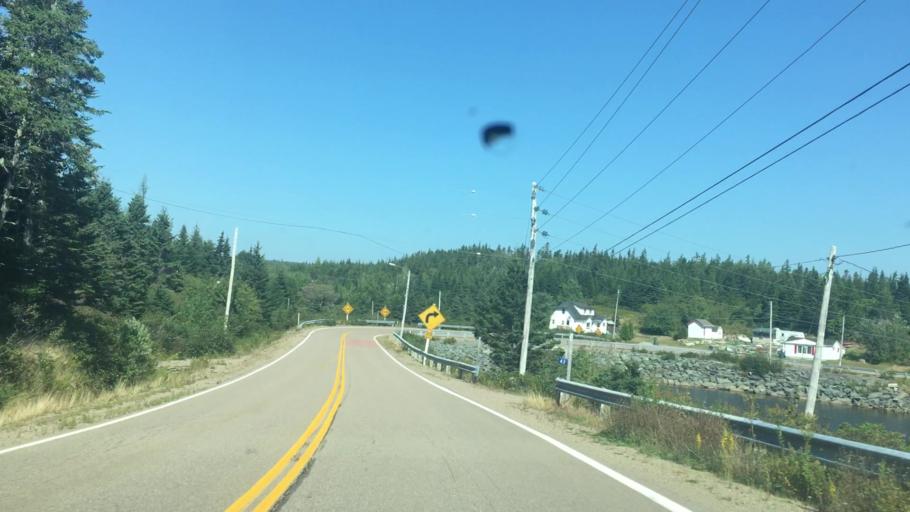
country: CA
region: Nova Scotia
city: Antigonish
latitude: 45.0268
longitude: -62.0308
